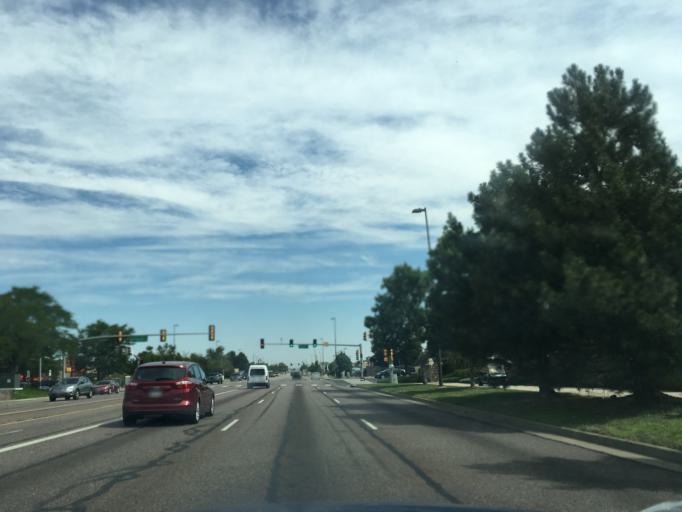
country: US
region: Colorado
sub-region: Adams County
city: Aurora
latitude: 39.6885
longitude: -104.8659
